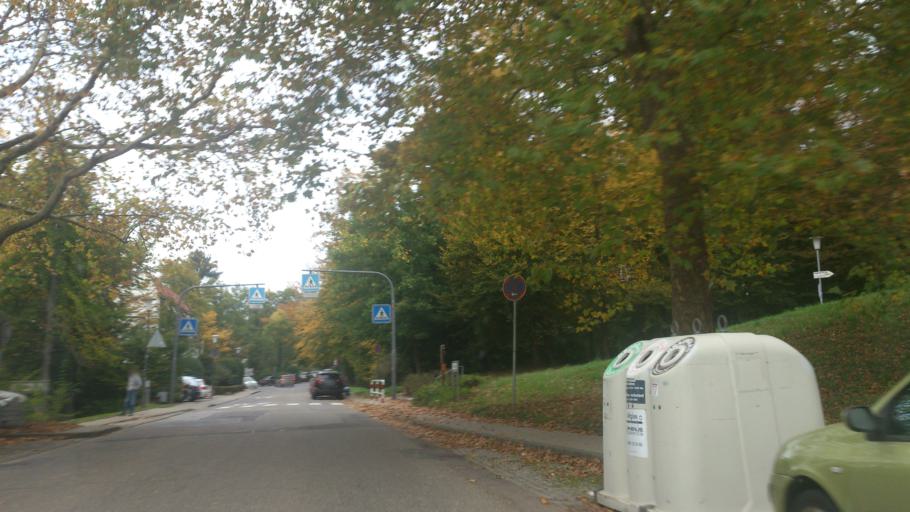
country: DE
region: Baden-Wuerttemberg
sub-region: Karlsruhe Region
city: Heidelberg
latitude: 49.3771
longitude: 8.7039
